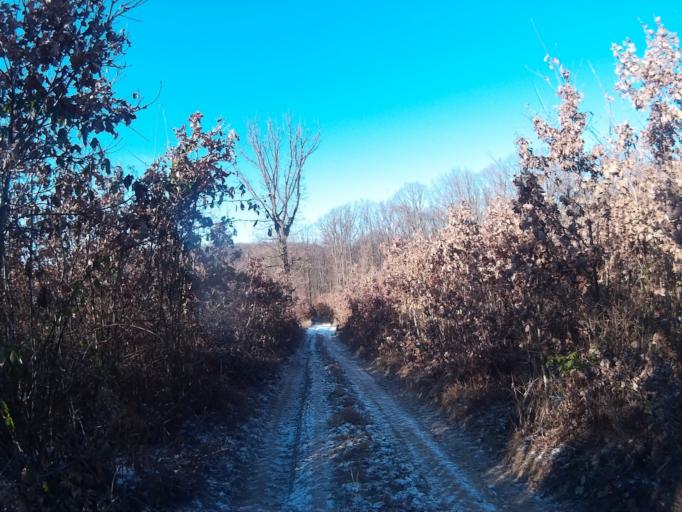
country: HU
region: Borsod-Abauj-Zemplen
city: Putnok
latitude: 48.4155
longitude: 20.4800
